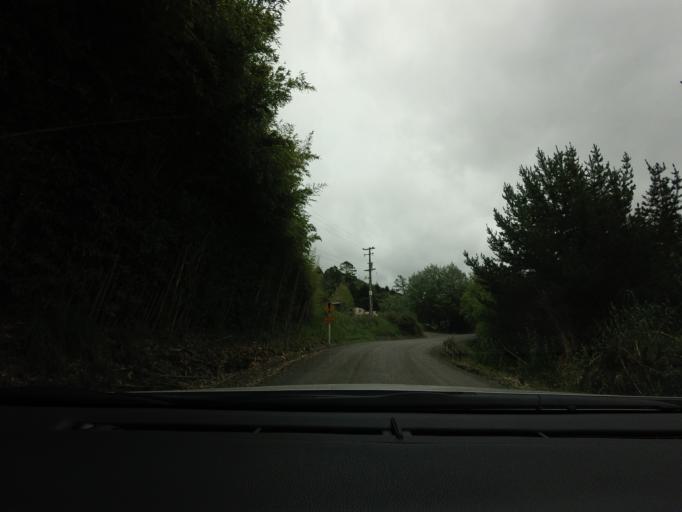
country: NZ
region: Auckland
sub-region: Auckland
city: Warkworth
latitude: -36.4891
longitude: 174.6192
